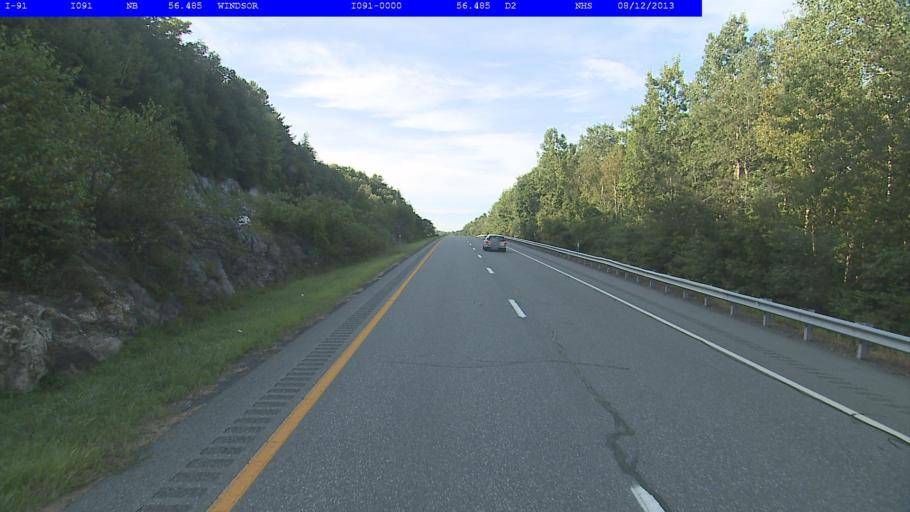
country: US
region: Vermont
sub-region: Windsor County
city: Windsor
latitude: 43.4730
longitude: -72.4061
